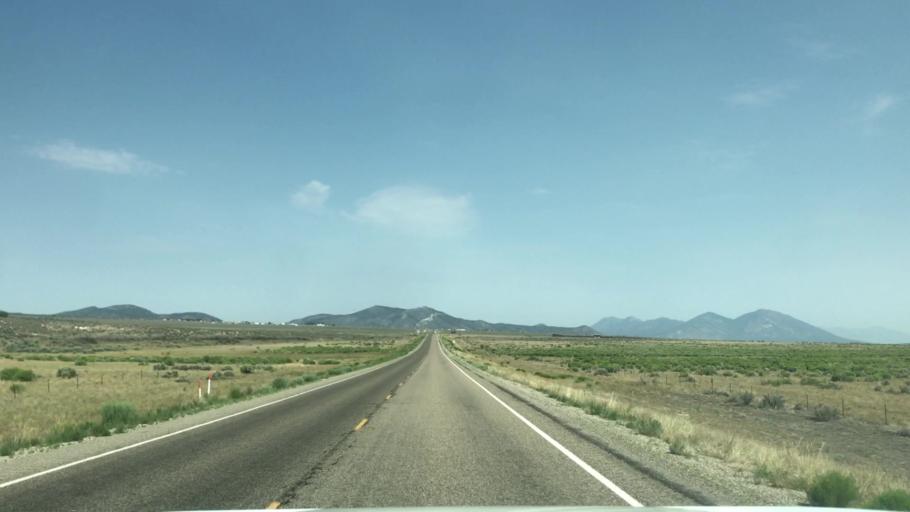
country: US
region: Nevada
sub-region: White Pine County
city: Ely
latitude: 39.1751
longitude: -114.8237
